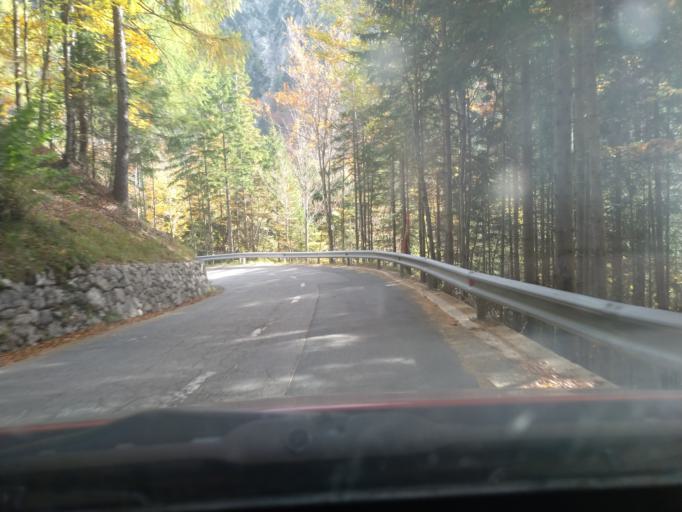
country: SI
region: Kranjska Gora
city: Kranjska Gora
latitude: 46.4076
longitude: 13.7539
